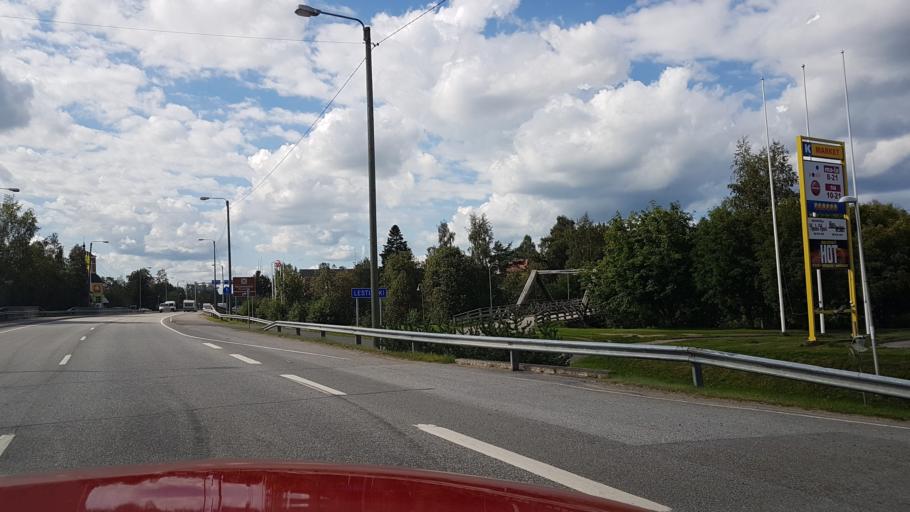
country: FI
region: Northern Ostrobothnia
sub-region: Ylivieska
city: Himanka
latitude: 64.0636
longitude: 23.6566
